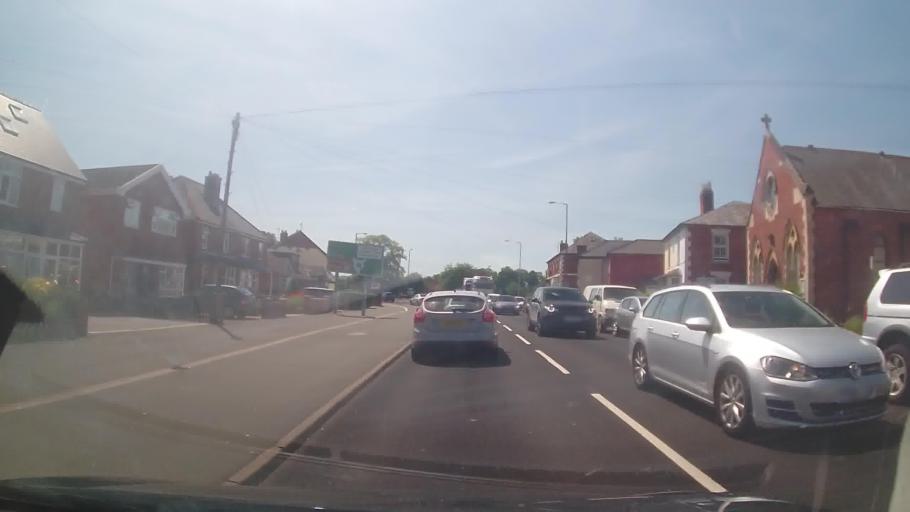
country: GB
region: England
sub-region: Herefordshire
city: Hereford
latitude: 52.0670
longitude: -2.7218
